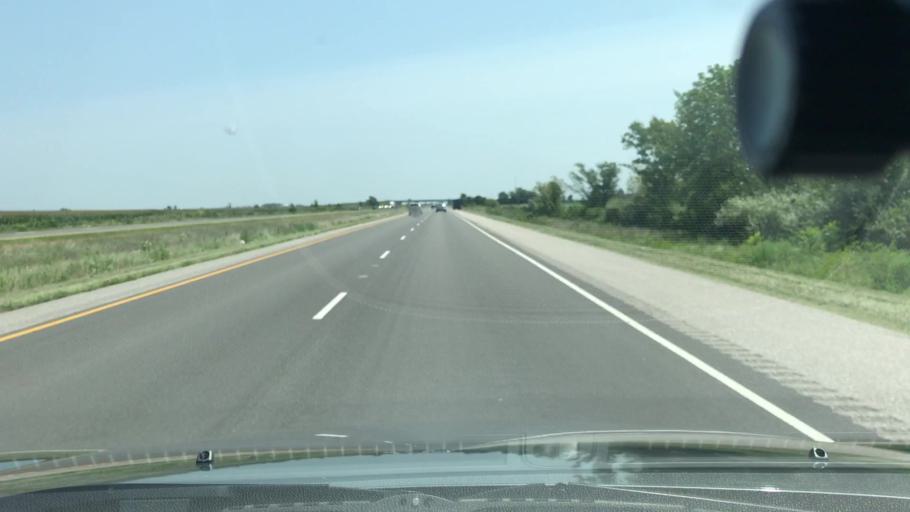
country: US
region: Illinois
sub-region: Washington County
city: Nashville
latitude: 38.3912
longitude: -89.2865
